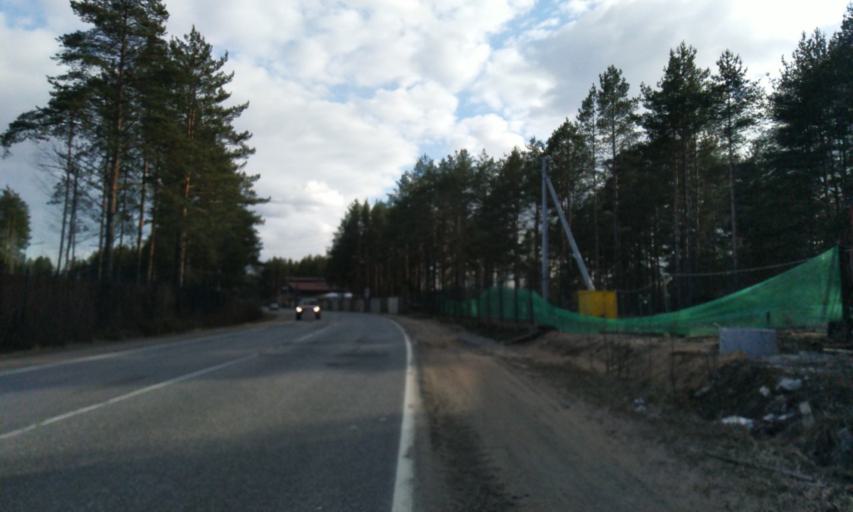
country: RU
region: Leningrad
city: Novoye Devyatkino
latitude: 60.1206
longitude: 30.4487
